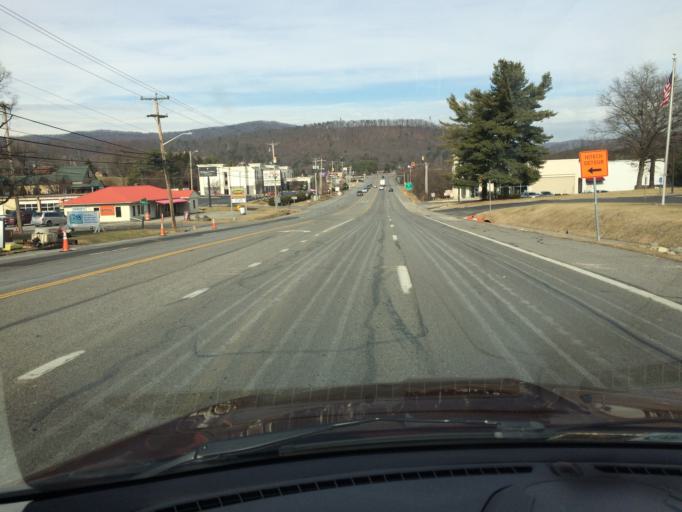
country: US
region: Virginia
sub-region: Roanoke County
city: Hollins
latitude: 37.3544
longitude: -79.9549
